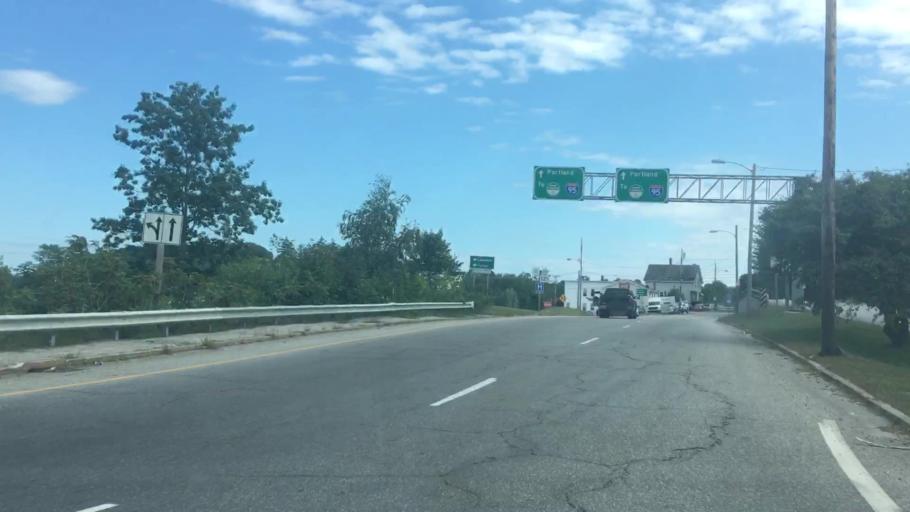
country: US
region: Maine
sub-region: Androscoggin County
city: Auburn
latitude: 44.0883
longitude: -70.2332
